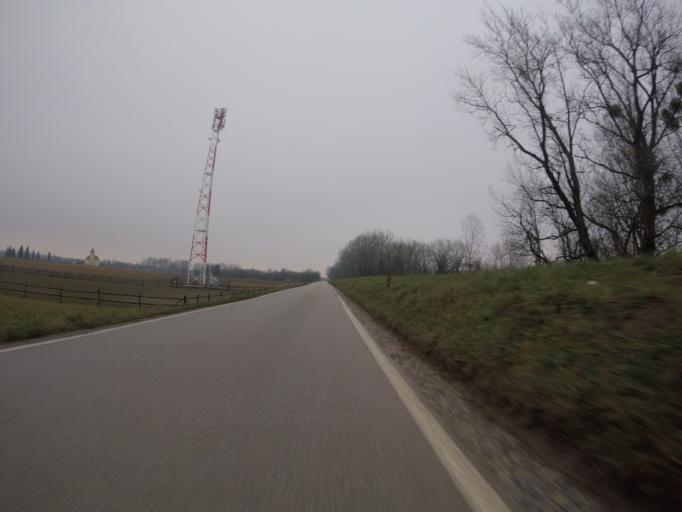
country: HR
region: Zagrebacka
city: Kuce
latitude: 45.6886
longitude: 16.2432
